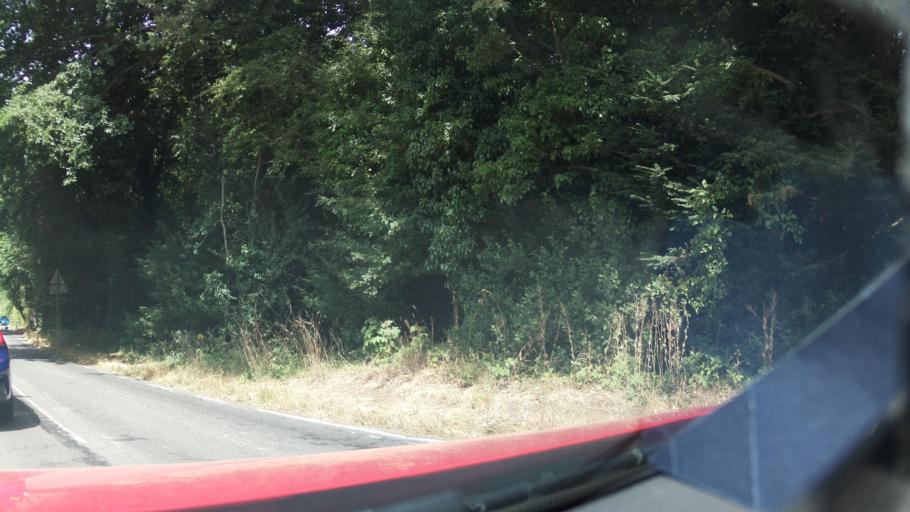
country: GB
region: England
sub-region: Surrey
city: Chilworth
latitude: 51.2407
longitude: -0.5202
